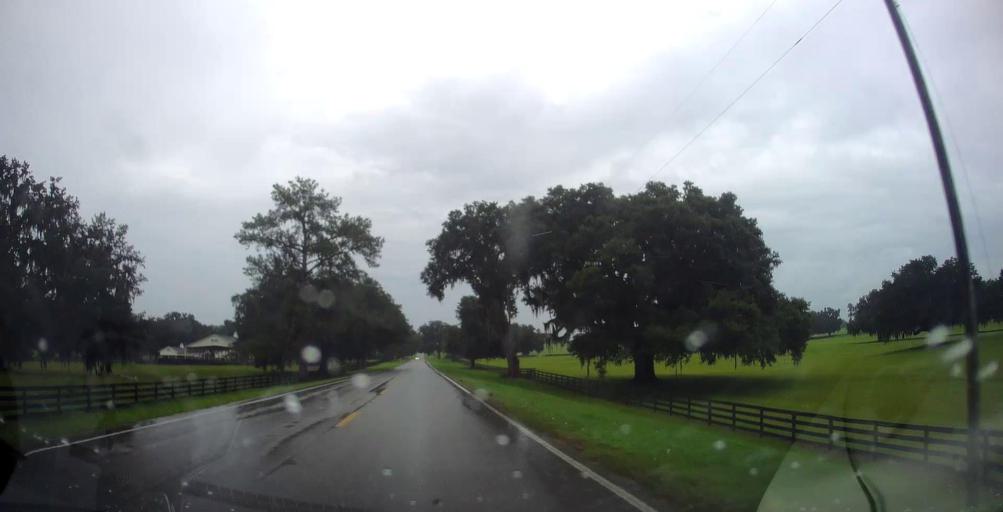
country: US
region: Florida
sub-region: Marion County
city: Citra
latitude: 29.3541
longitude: -82.2348
